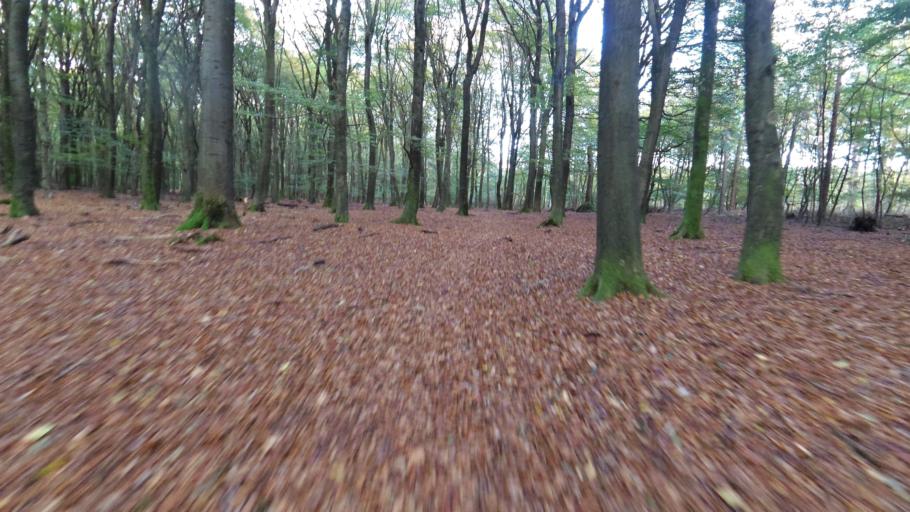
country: NL
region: Gelderland
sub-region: Gemeente Nunspeet
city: Nunspeet
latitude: 52.3172
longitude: 5.8357
